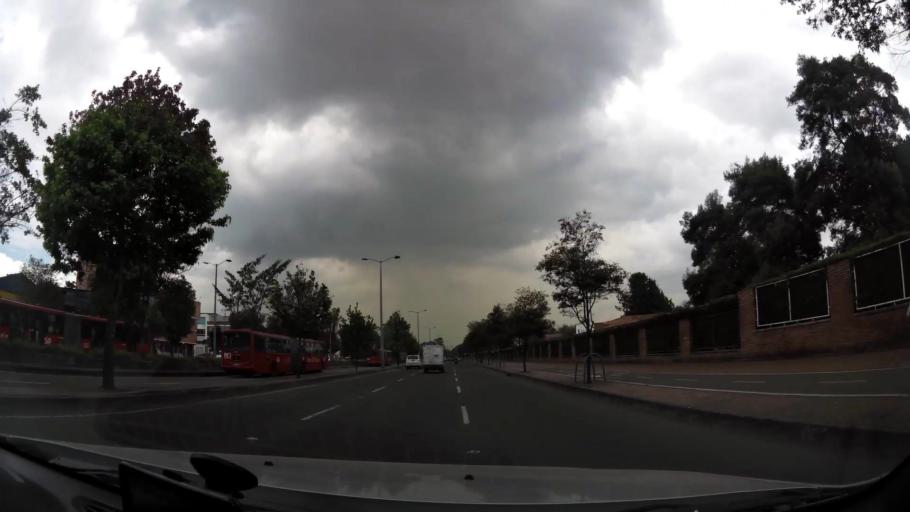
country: CO
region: Bogota D.C.
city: Barrio San Luis
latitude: 4.6774
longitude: -74.0724
